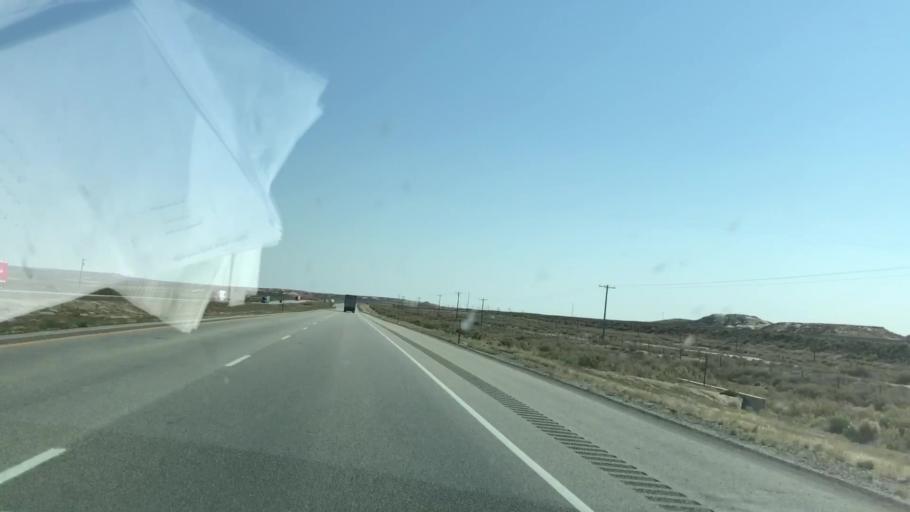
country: US
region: Wyoming
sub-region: Carbon County
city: Rawlins
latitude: 41.6994
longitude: -107.9105
